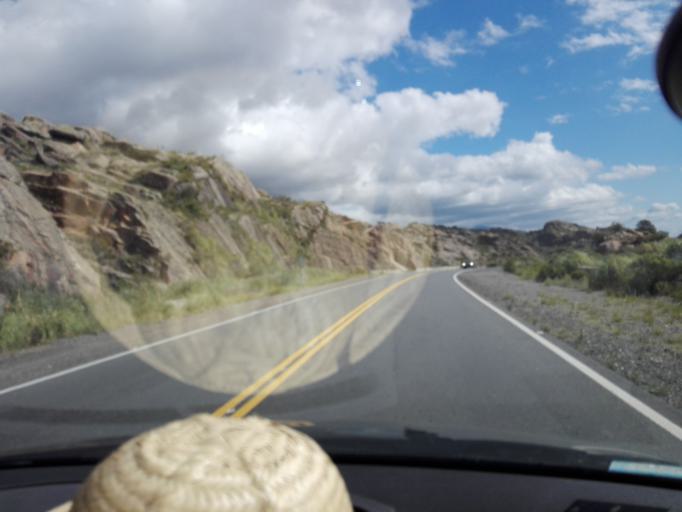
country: AR
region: Cordoba
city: Mina Clavero
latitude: -31.7577
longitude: -64.9129
